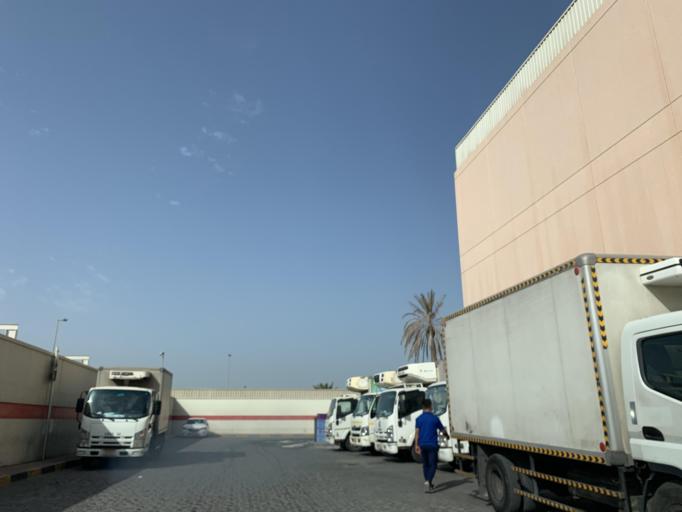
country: BH
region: Northern
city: Sitrah
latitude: 26.1685
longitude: 50.6007
